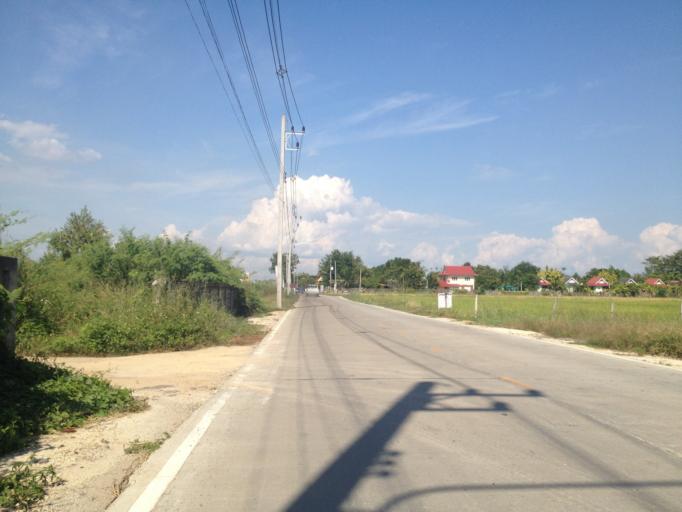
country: TH
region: Chiang Mai
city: Hang Dong
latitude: 18.7118
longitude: 98.9676
